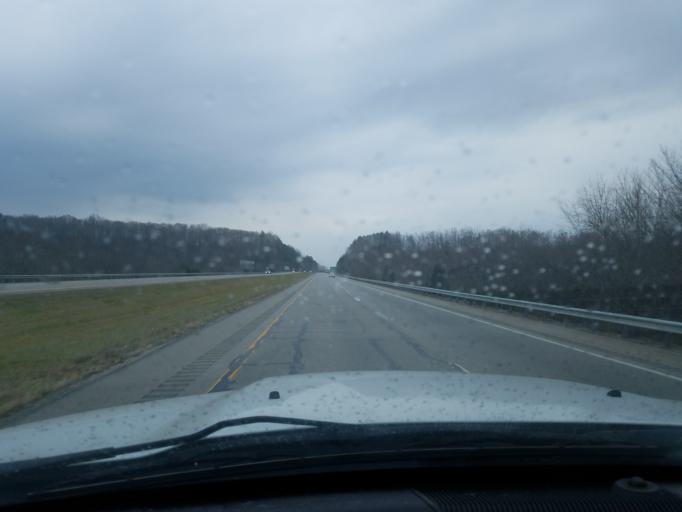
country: US
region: Kentucky
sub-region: Rowan County
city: Morehead
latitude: 38.1868
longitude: -83.5015
